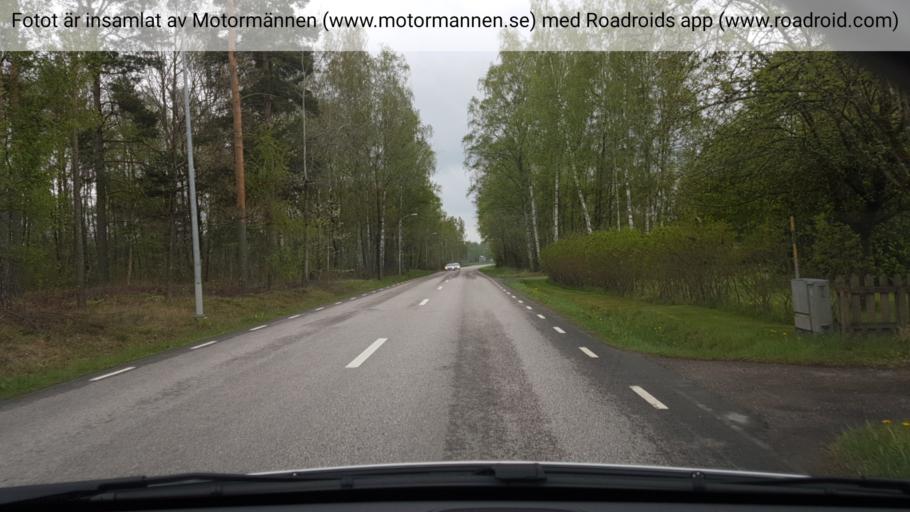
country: SE
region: Vaestra Goetaland
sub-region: Skovde Kommun
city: Stopen
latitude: 58.5613
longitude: 14.0076
